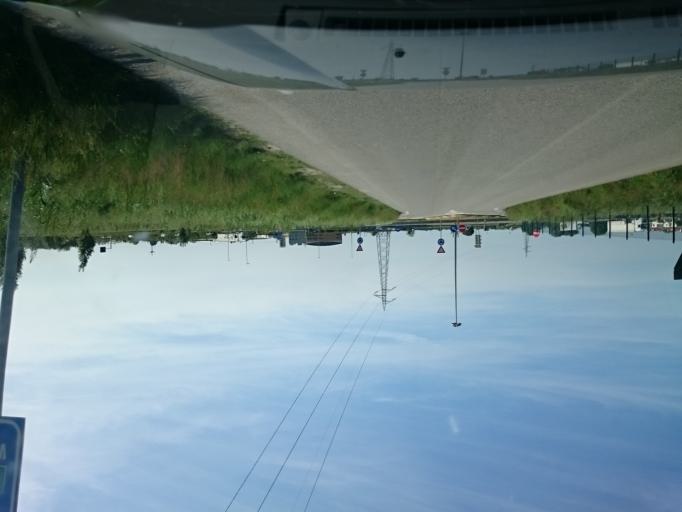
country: IT
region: Veneto
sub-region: Provincia di Venezia
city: Fornase
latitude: 45.4347
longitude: 12.1898
